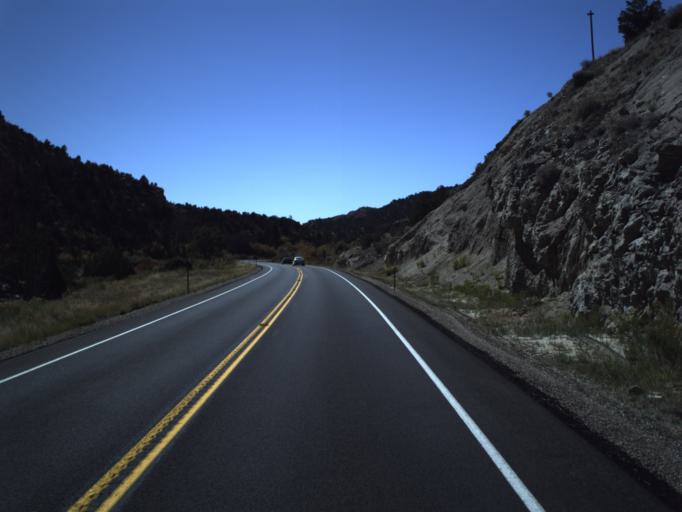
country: US
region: Utah
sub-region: Garfield County
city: Panguitch
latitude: 37.6069
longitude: -111.9065
